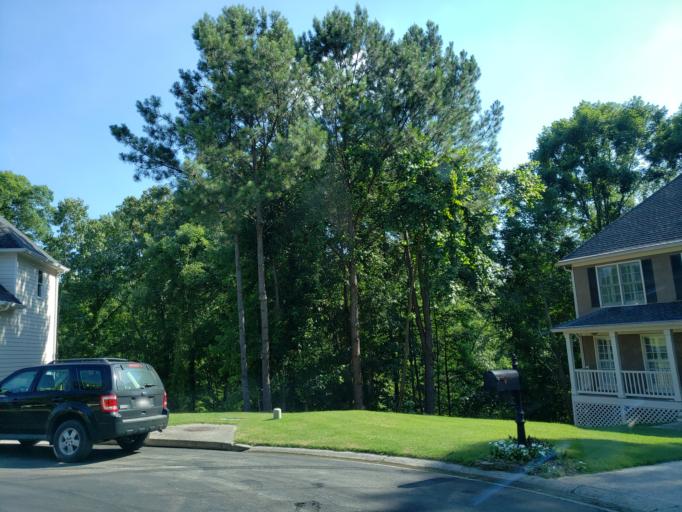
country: US
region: Georgia
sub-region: Cherokee County
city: Woodstock
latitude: 34.1230
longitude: -84.5345
